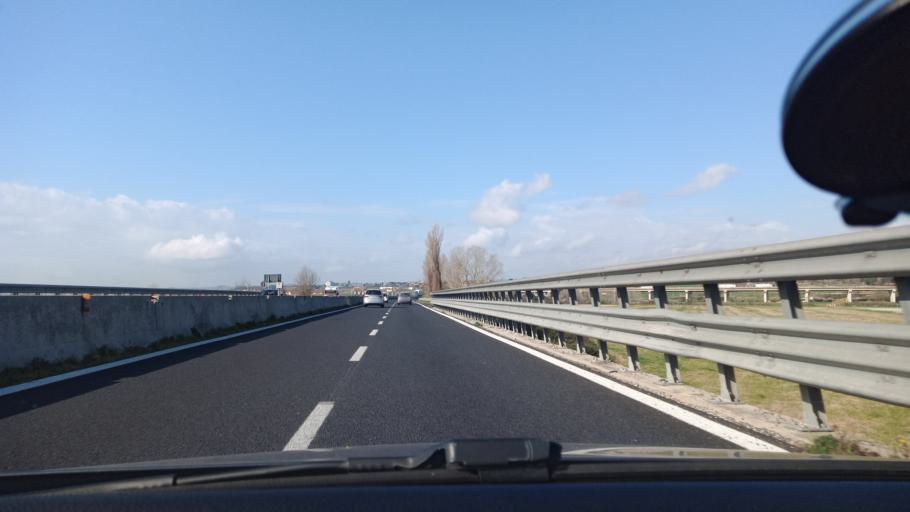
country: IT
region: Latium
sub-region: Citta metropolitana di Roma Capitale
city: Fiano Romano
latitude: 42.1509
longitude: 12.6349
